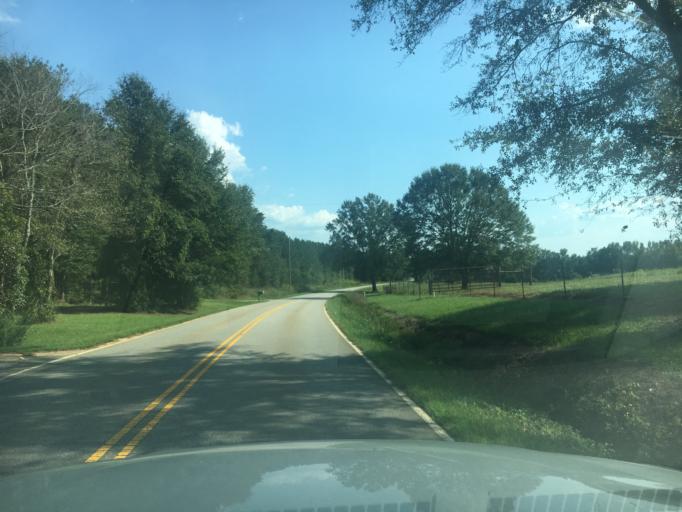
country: US
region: South Carolina
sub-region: Pickens County
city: Liberty
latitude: 34.7317
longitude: -82.6410
